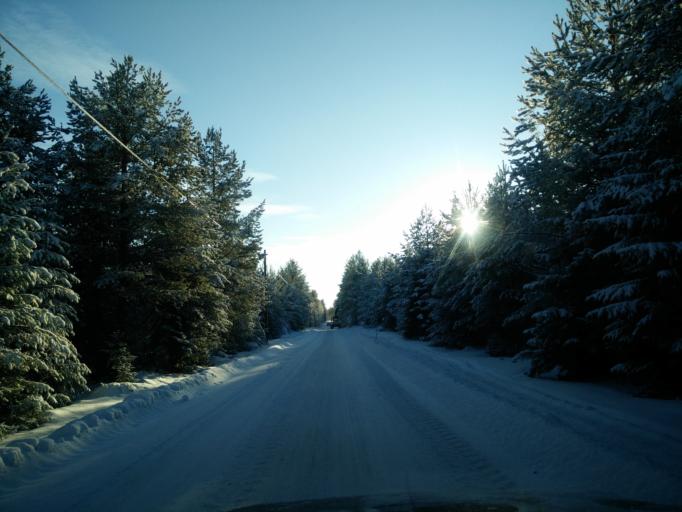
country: SE
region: Vaesternorrland
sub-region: Sundsvalls Kommun
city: Njurundabommen
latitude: 62.2158
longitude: 17.4935
